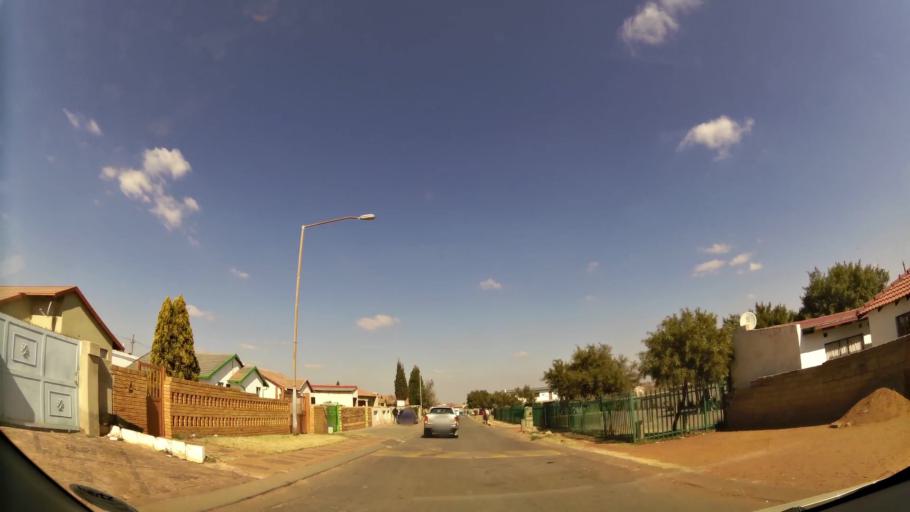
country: ZA
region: Gauteng
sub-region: West Rand District Municipality
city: Krugersdorp
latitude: -26.1495
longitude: 27.7719
